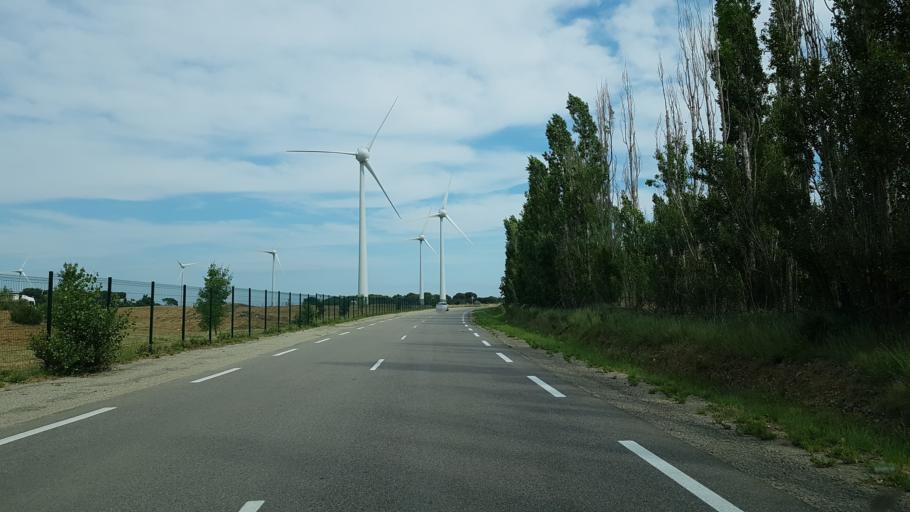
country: FR
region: Provence-Alpes-Cote d'Azur
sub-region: Departement des Bouches-du-Rhone
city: Saint-Martin-de-Crau
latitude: 43.6227
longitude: 4.7599
